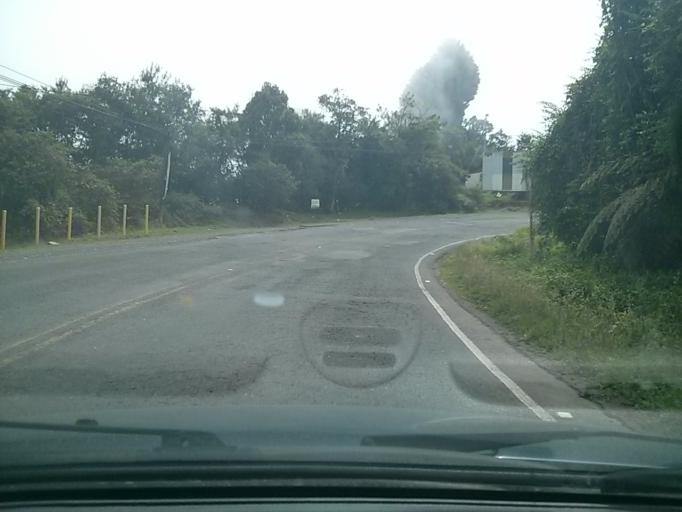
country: CR
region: San Jose
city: San Marcos
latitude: 9.7353
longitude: -83.9500
